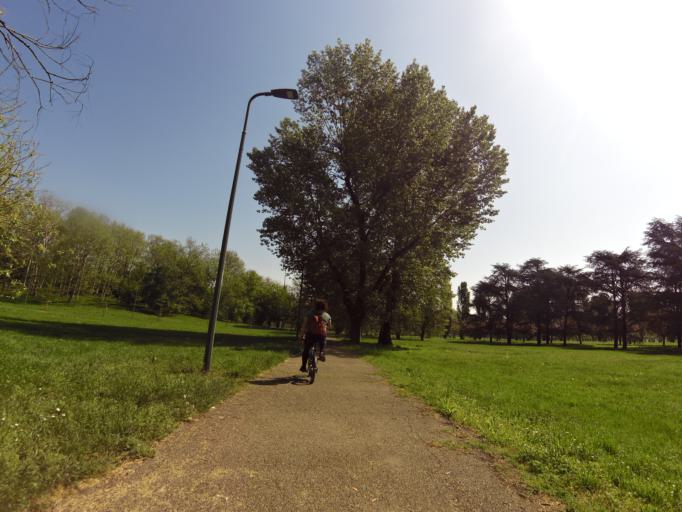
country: IT
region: Lombardy
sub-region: Citta metropolitana di Milano
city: Novegro-Tregarezzo-San Felice
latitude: 45.4650
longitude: 9.2590
